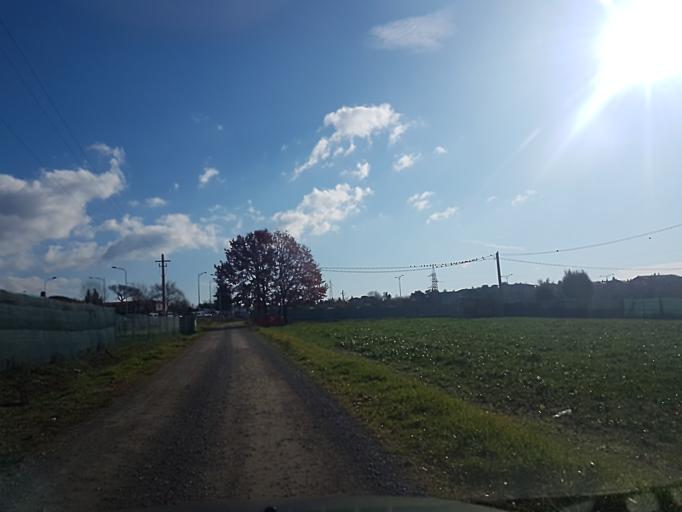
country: IT
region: Umbria
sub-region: Provincia di Perugia
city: Lacugnano
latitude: 43.0766
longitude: 12.3524
